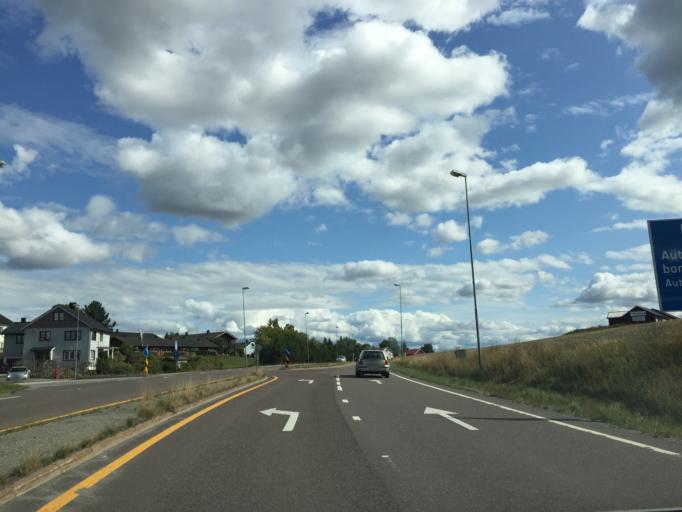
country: NO
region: Ostfold
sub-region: Spydeberg
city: Spydeberg
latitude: 59.6143
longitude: 11.0811
